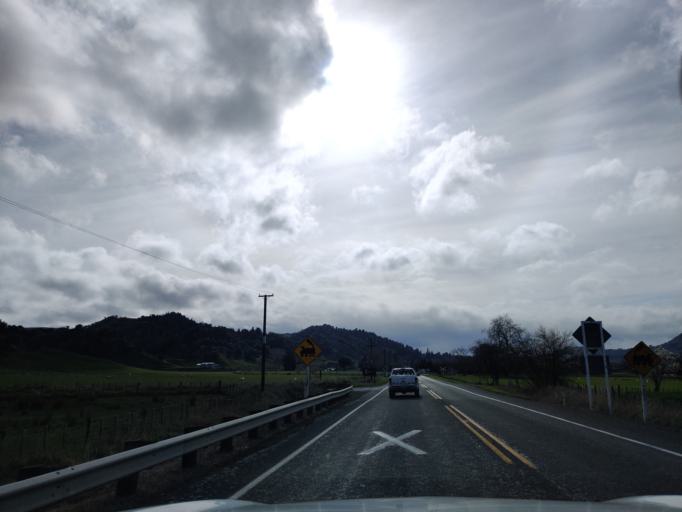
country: NZ
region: Manawatu-Wanganui
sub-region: Ruapehu District
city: Waiouru
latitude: -39.8210
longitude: 175.7773
